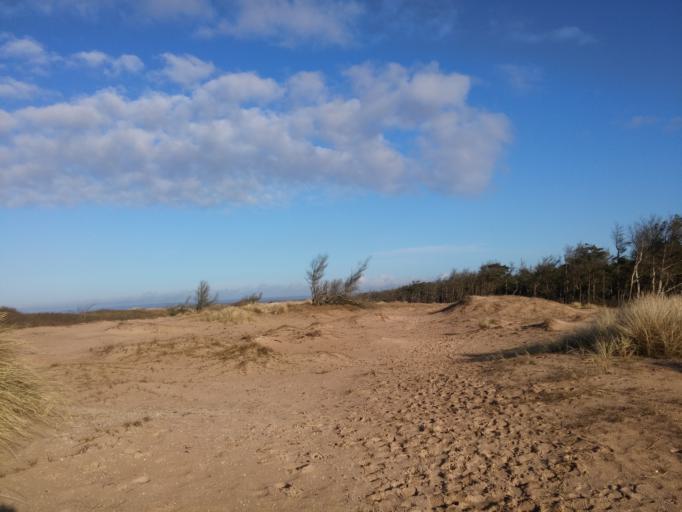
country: SE
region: Skane
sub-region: Angelholms Kommun
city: AEngelholm
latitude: 56.2384
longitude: 12.8168
